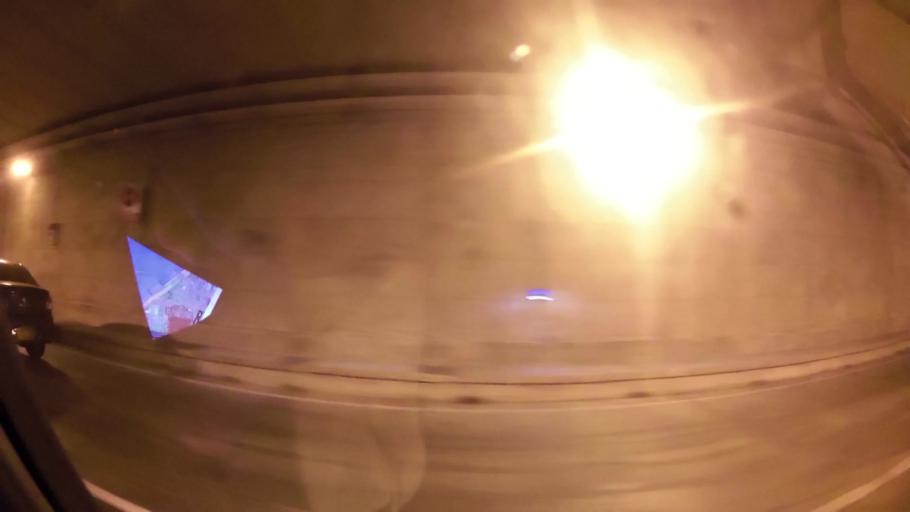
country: CO
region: Bolivar
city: Cartagena
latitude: 10.4481
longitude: -75.5221
